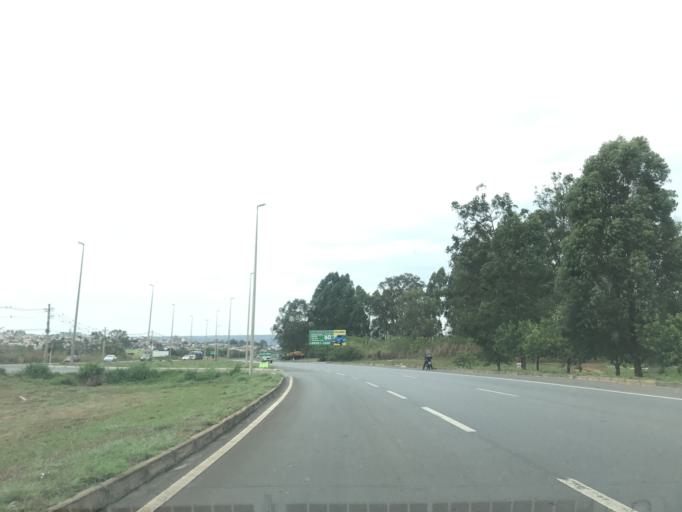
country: BR
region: Federal District
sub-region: Brasilia
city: Brasilia
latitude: -15.6844
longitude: -47.8538
